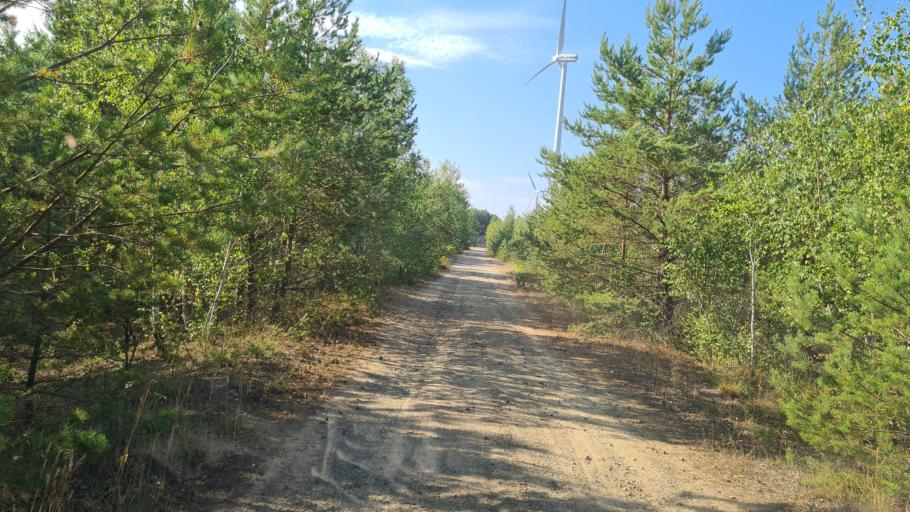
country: DE
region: Brandenburg
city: Sallgast
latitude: 51.5626
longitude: 13.8440
